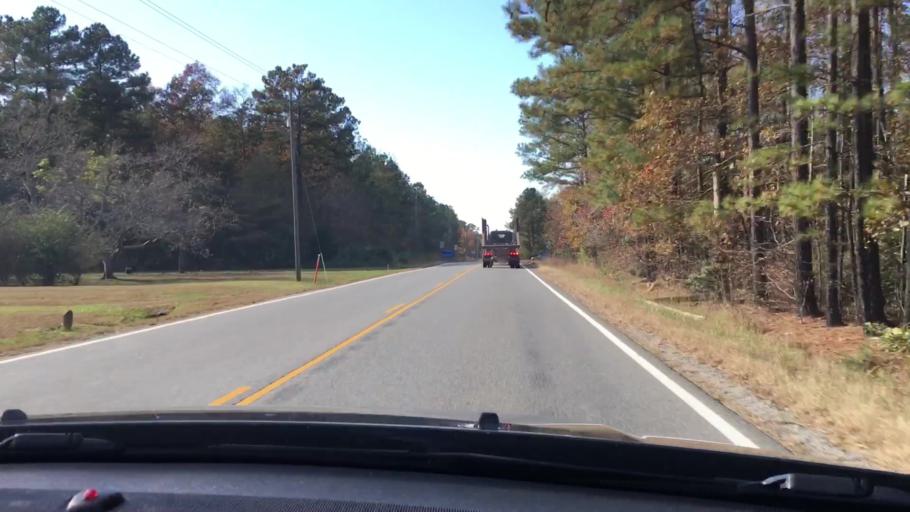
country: US
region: Virginia
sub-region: Hanover County
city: Hanover
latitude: 37.8260
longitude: -77.3366
